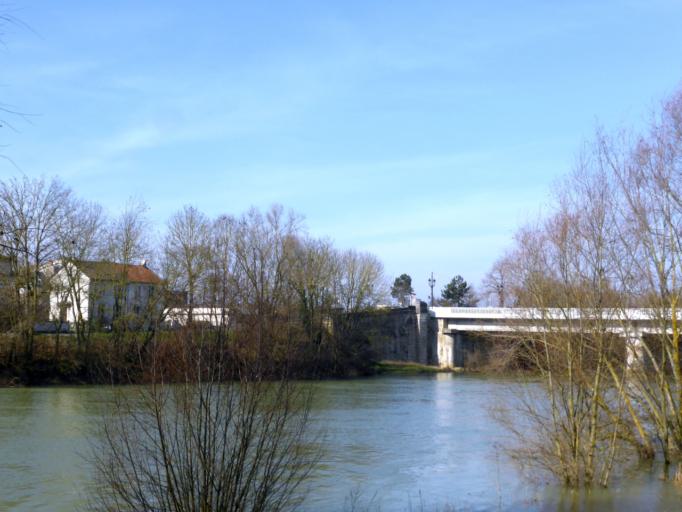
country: FR
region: Champagne-Ardenne
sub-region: Departement de la Marne
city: Compertrix
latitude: 48.9530
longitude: 4.3530
